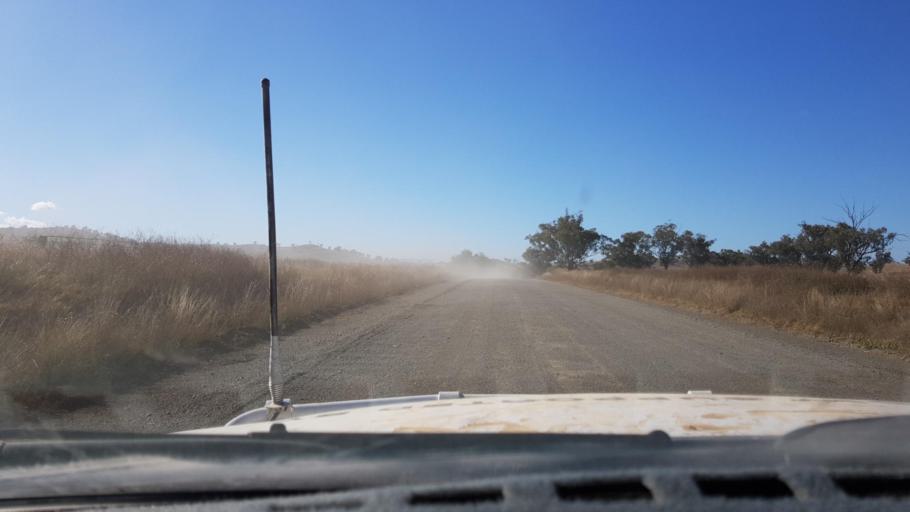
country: AU
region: New South Wales
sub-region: Narrabri
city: Blair Athol
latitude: -30.6692
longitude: 150.3785
